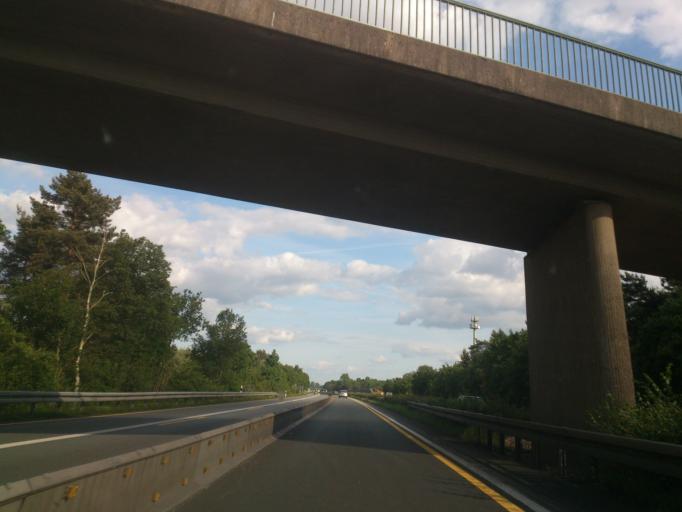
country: DE
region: North Rhine-Westphalia
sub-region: Regierungsbezirk Detmold
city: Hovelhof
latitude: 51.8431
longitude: 8.6789
